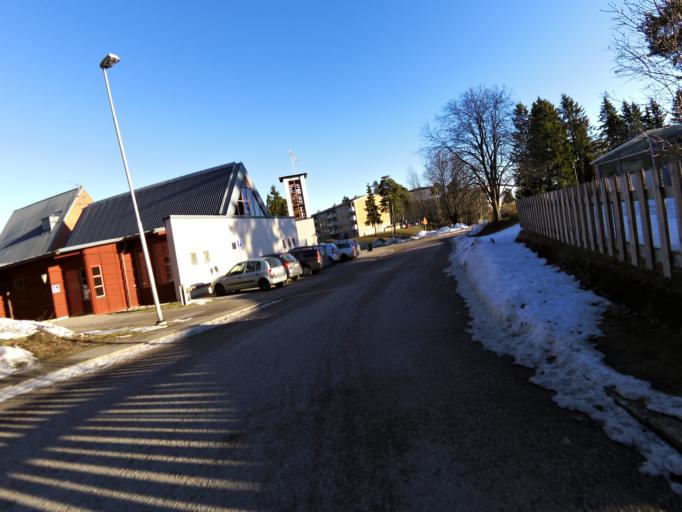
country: SE
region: Gaevleborg
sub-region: Gavle Kommun
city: Gavle
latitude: 60.6586
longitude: 17.1456
